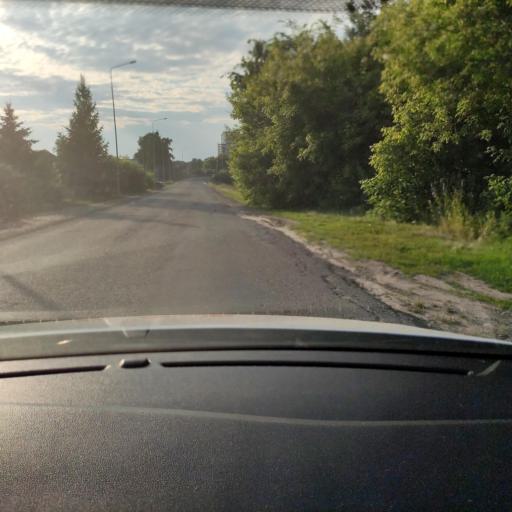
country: RU
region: Tatarstan
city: Vysokaya Gora
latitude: 55.9768
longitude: 49.3083
